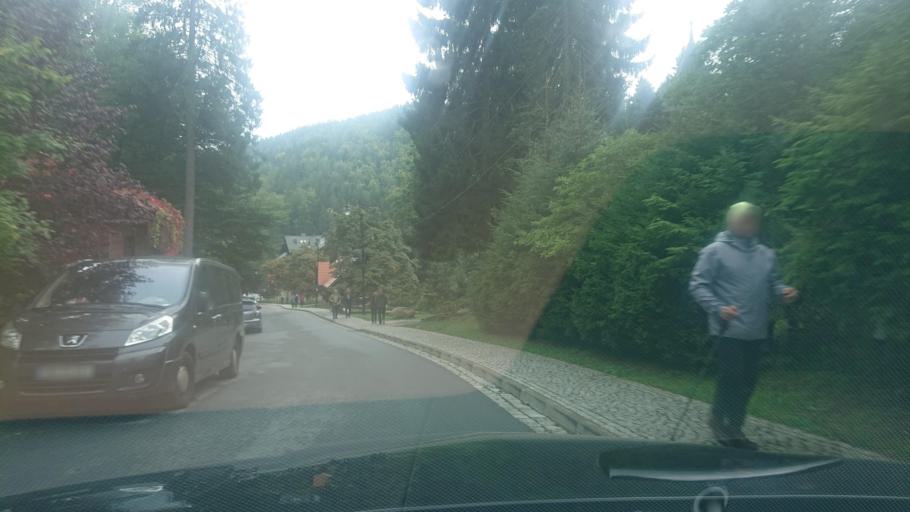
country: PL
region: Lower Silesian Voivodeship
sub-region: Powiat klodzki
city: Stronie Slaskie
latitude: 50.2306
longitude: 16.7661
